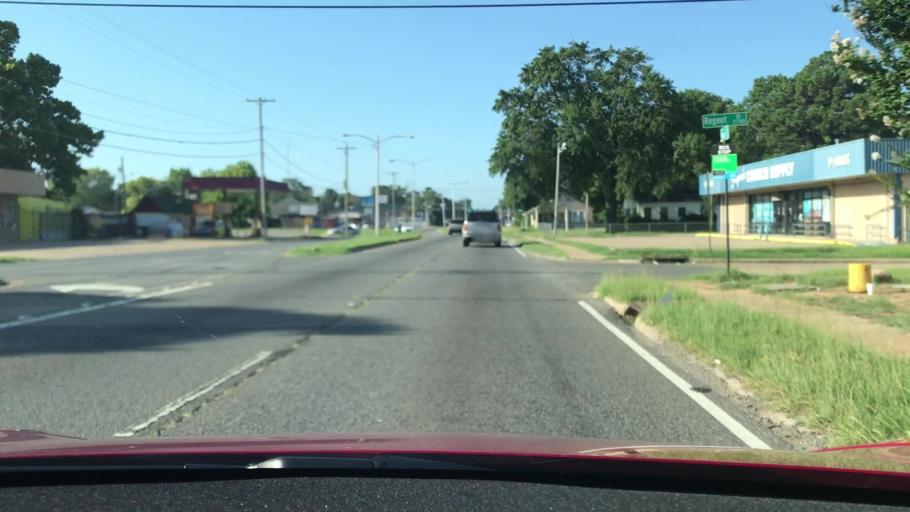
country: US
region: Louisiana
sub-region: Caddo Parish
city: Shreveport
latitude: 32.4738
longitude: -93.7801
